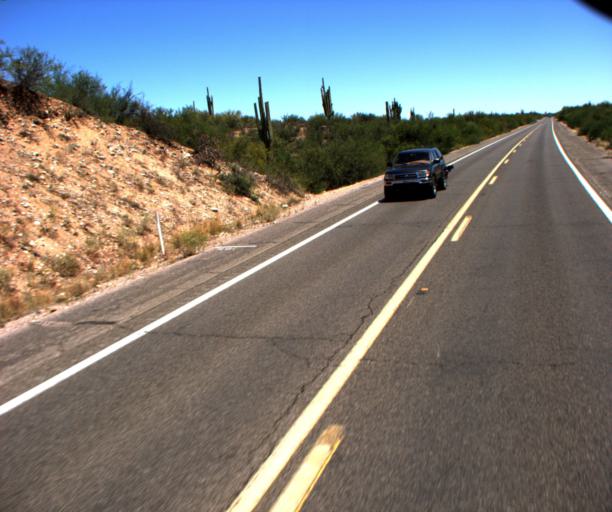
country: US
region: Arizona
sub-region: Pinal County
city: Mammoth
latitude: 32.8289
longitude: -110.6997
